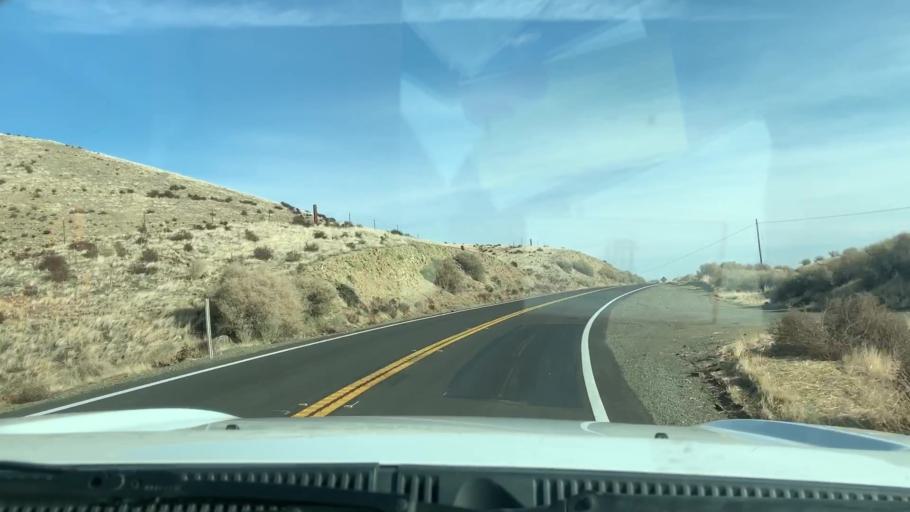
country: US
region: California
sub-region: Fresno County
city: Coalinga
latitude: 36.1097
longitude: -120.3935
